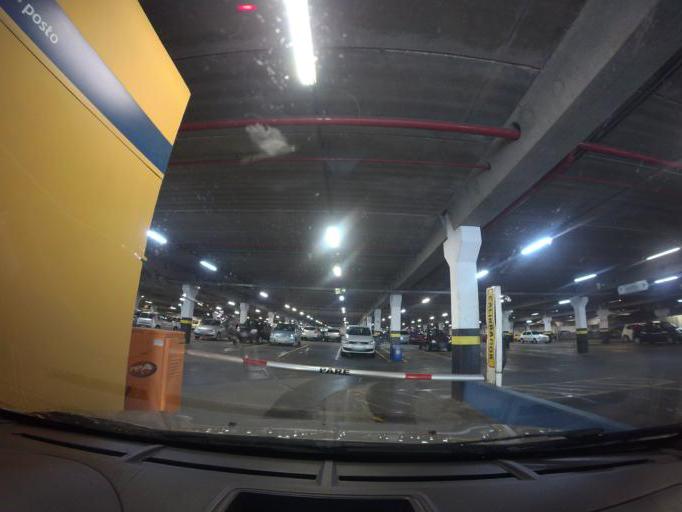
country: BR
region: Sao Paulo
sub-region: Piracicaba
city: Piracicaba
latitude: -22.7367
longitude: -47.6480
